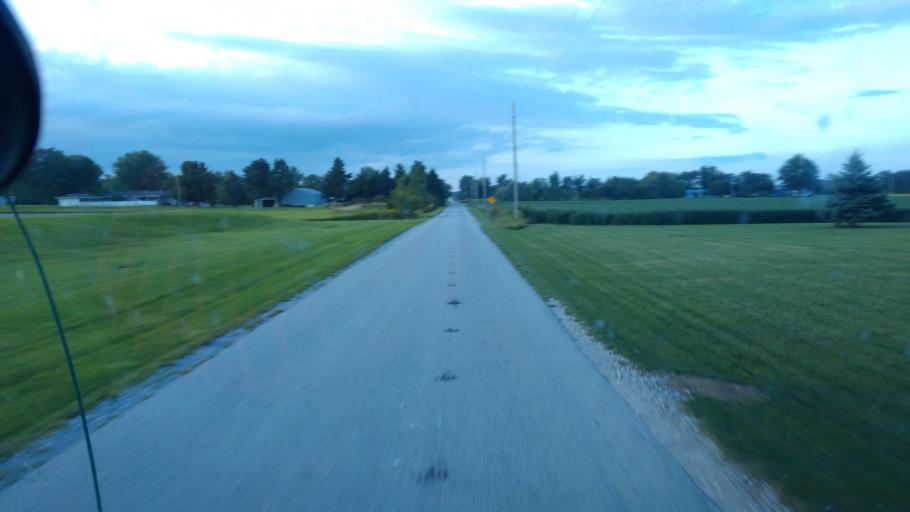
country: US
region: Ohio
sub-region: Hardin County
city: Kenton
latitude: 40.6405
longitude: -83.5152
